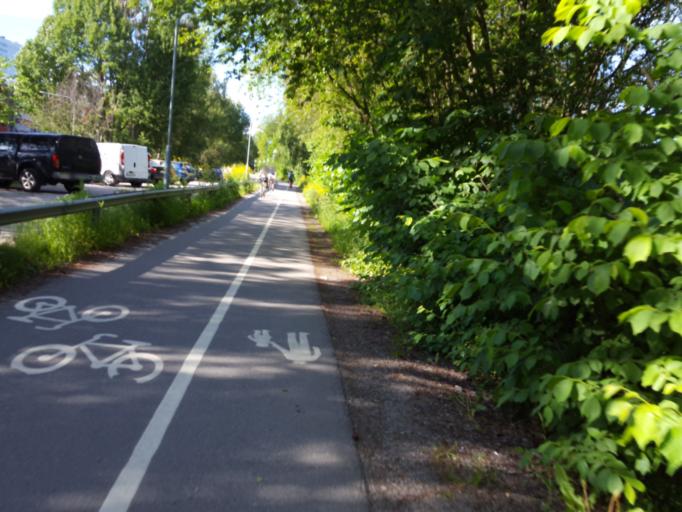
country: SE
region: Stockholm
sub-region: Solna Kommun
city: Solna
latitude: 59.3580
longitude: 18.0171
